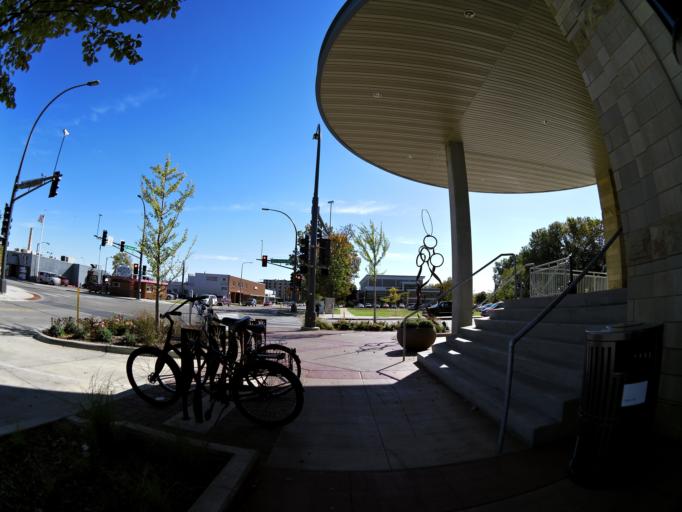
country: US
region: Minnesota
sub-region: Olmsted County
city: Rochester
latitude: 44.0415
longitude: -92.4217
